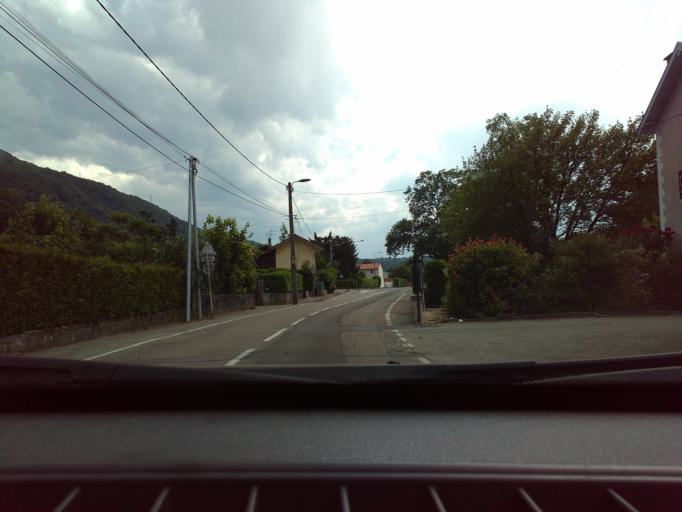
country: FR
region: Rhone-Alpes
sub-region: Departement de l'Isere
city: Saint-Martin-d'Heres
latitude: 45.1690
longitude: 5.7685
